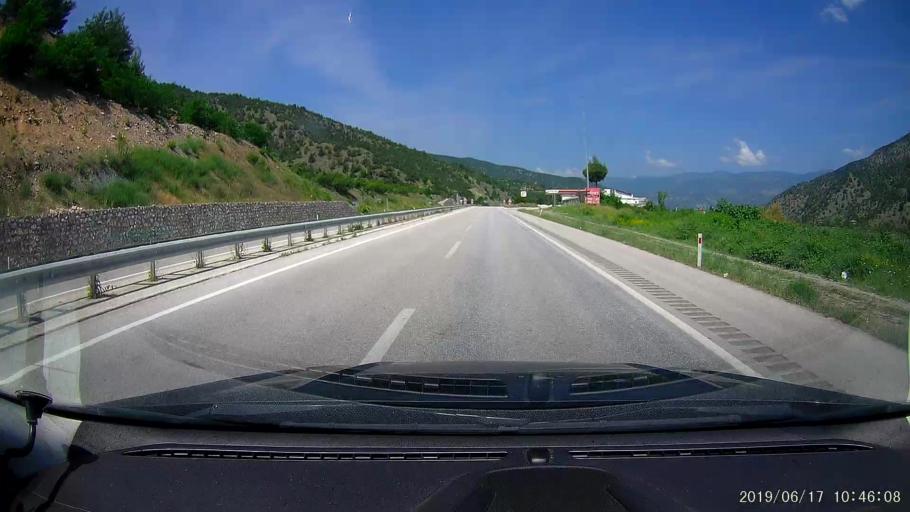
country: TR
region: Corum
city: Hacihamza
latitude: 41.0652
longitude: 34.4696
